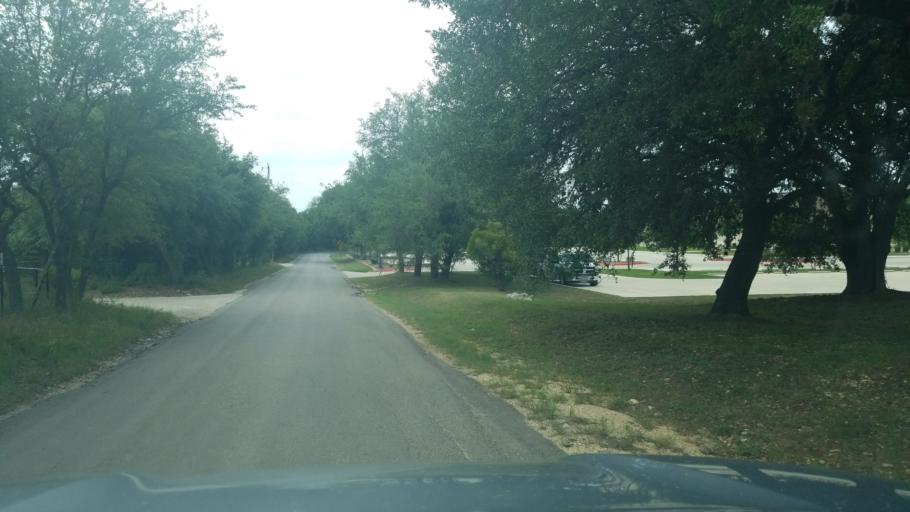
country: US
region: Texas
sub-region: Comal County
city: Bulverde
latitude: 29.7614
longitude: -98.4089
